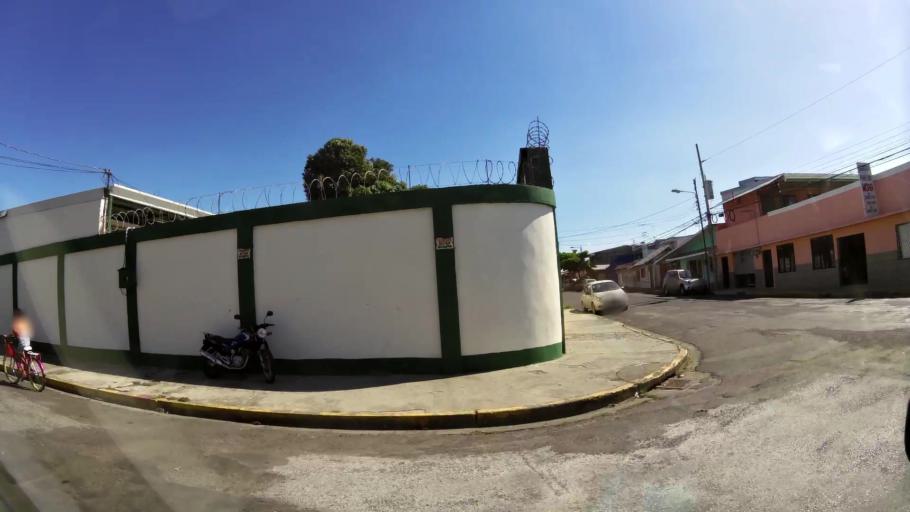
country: CR
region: Guanacaste
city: Liberia
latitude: 10.6330
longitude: -85.4401
